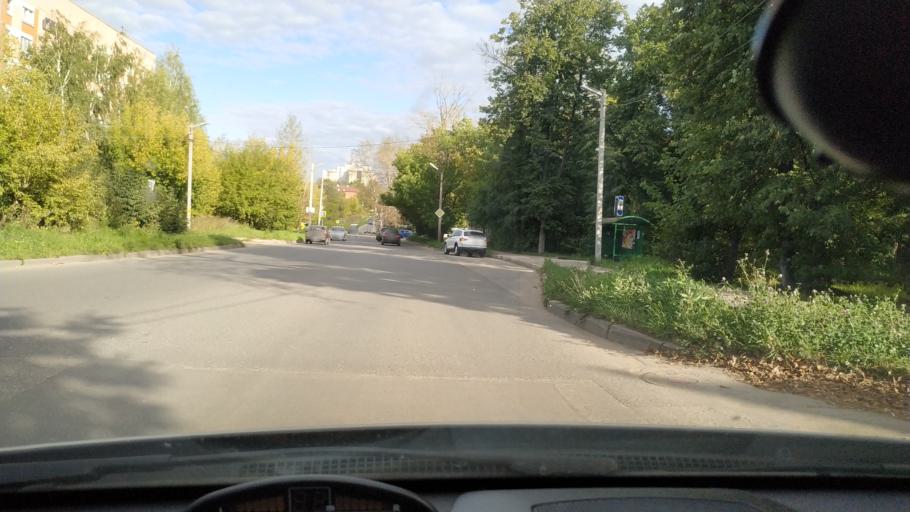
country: RU
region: Rjazan
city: Ryazan'
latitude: 54.6065
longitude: 39.7285
